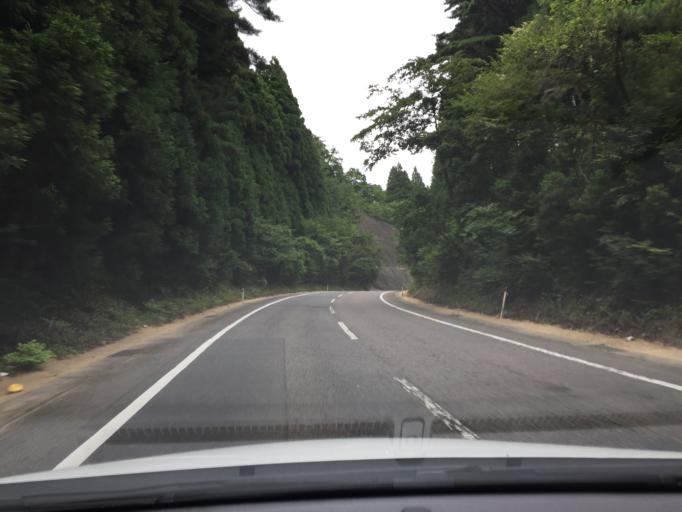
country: JP
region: Fukushima
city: Sukagawa
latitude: 37.1761
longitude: 140.1748
